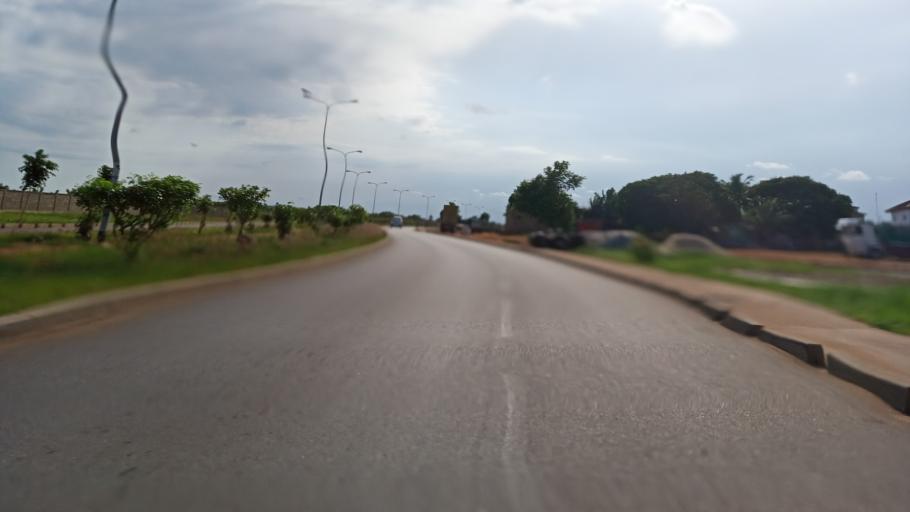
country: TG
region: Maritime
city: Lome
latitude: 6.1869
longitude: 1.2688
